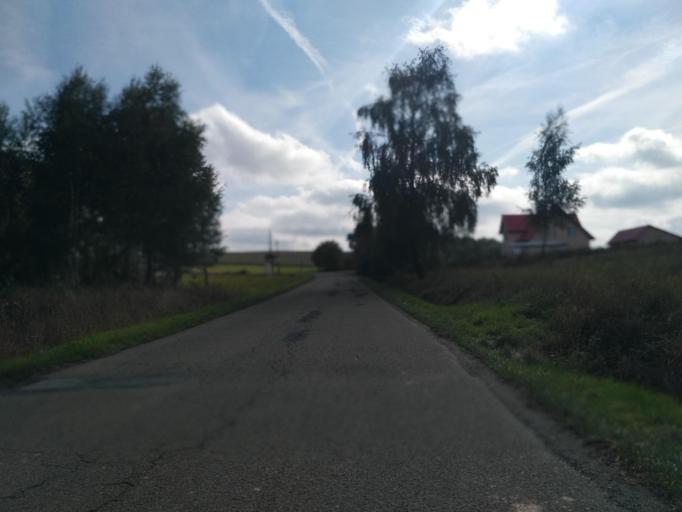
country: PL
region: Subcarpathian Voivodeship
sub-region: Powiat ropczycko-sedziszowski
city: Wielopole Skrzynskie
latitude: 49.9212
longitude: 21.5630
